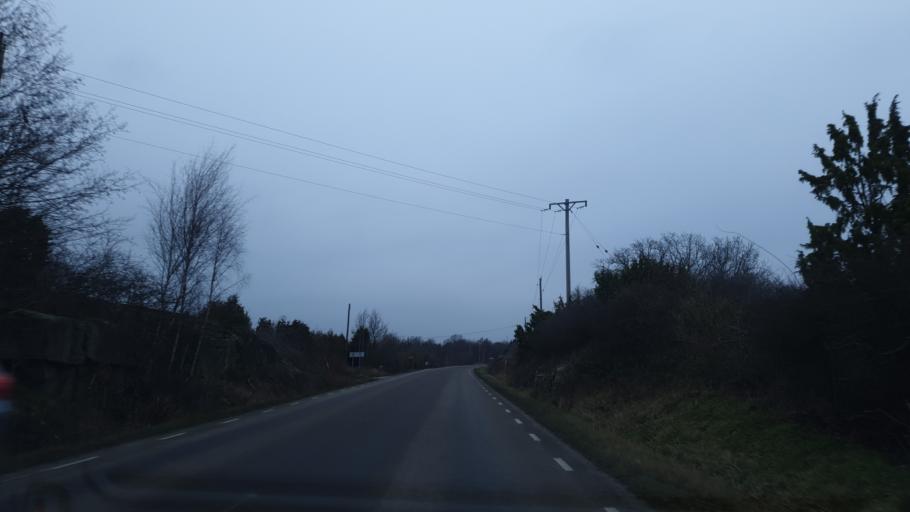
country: SE
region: Blekinge
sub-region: Karlskrona Kommun
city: Sturko
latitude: 56.1123
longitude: 15.7248
